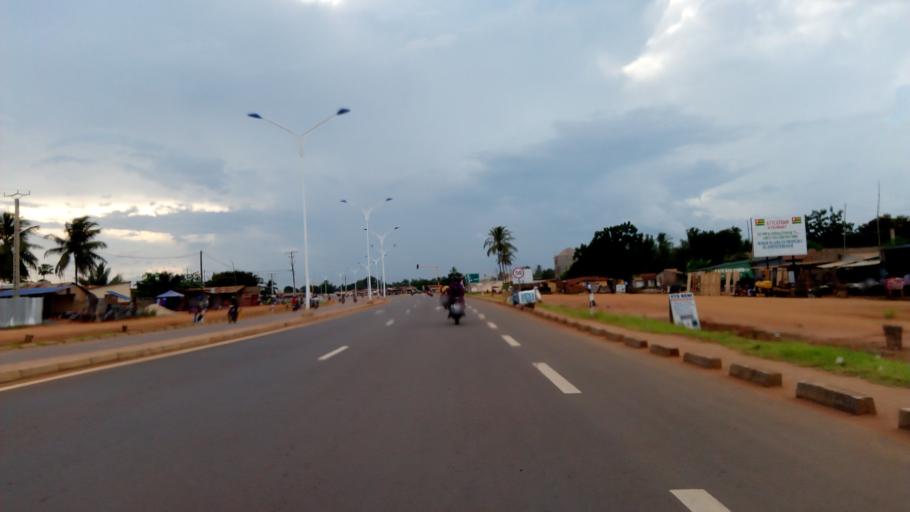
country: TG
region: Maritime
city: Lome
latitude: 6.2672
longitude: 1.1543
